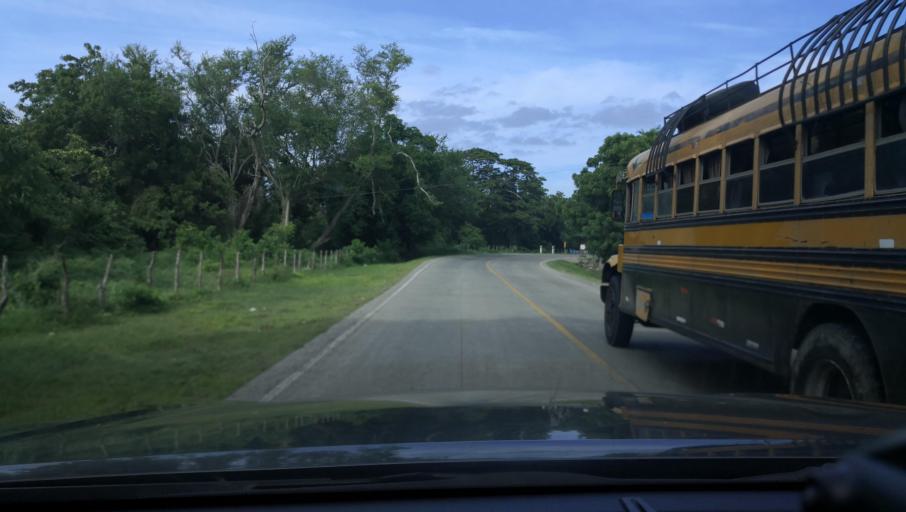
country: NI
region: Masaya
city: Tisma
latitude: 12.1530
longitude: -85.8312
